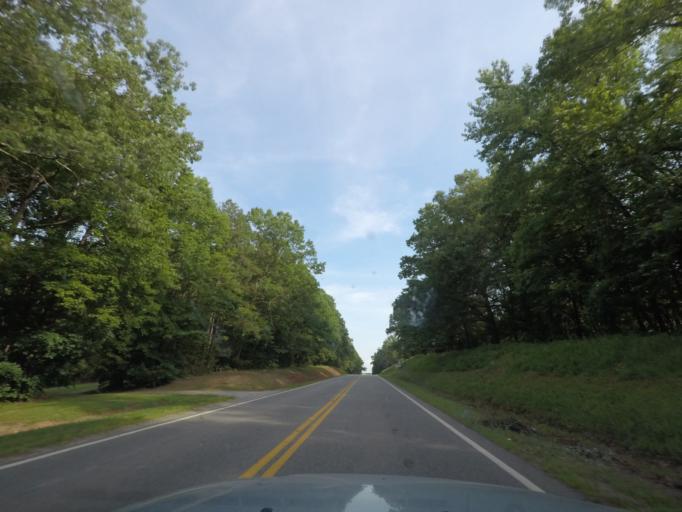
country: US
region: Virginia
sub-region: Mecklenburg County
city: Clarksville
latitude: 36.5951
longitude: -78.5491
